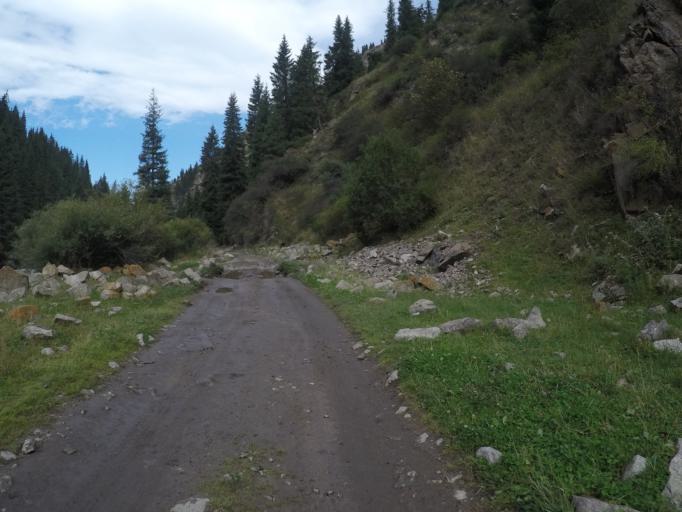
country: KG
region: Ysyk-Koel
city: Teploklyuchenka
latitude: 42.4407
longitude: 78.5568
